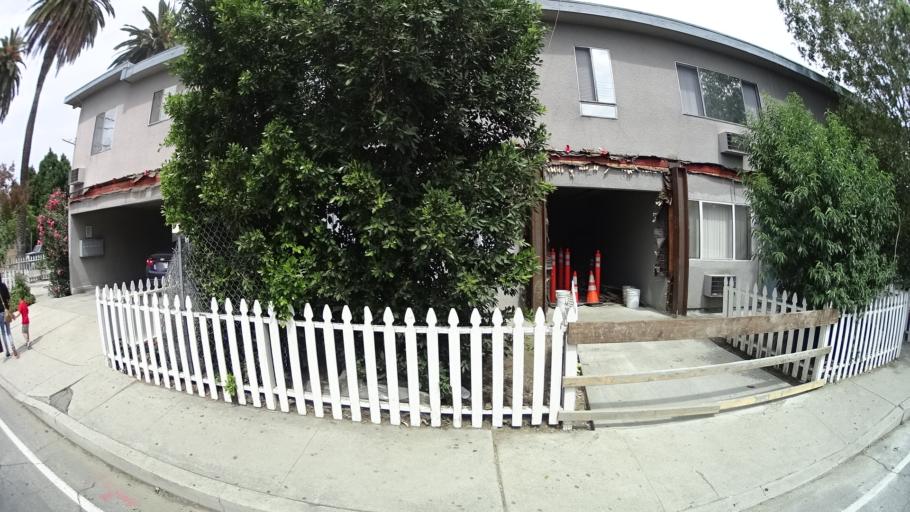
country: US
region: California
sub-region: Los Angeles County
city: Van Nuys
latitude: 34.1854
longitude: -118.4574
